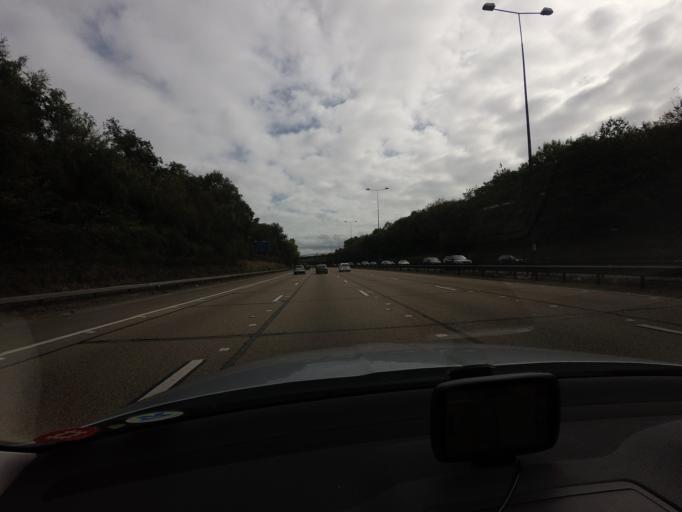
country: GB
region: England
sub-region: Surrey
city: Reigate
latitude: 51.2578
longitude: -0.2191
